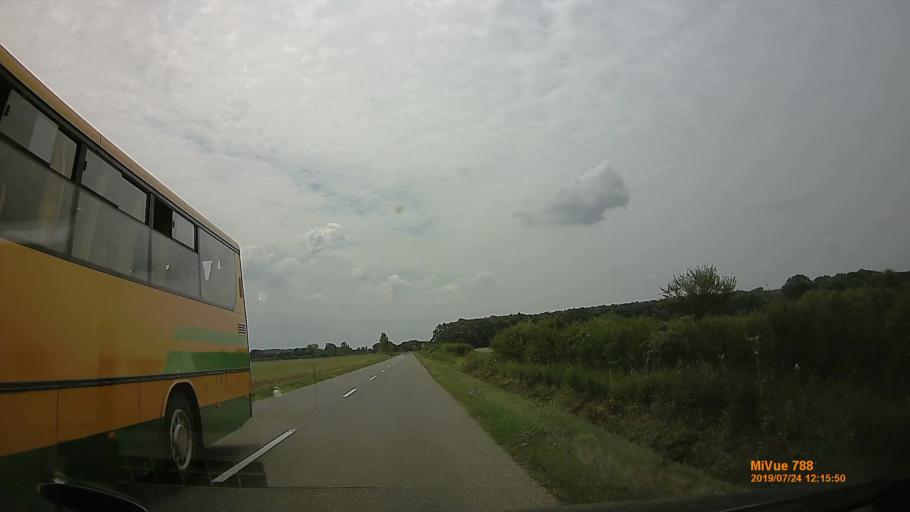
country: HU
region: Szabolcs-Szatmar-Bereg
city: Vasarosnameny
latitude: 48.1791
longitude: 22.3466
